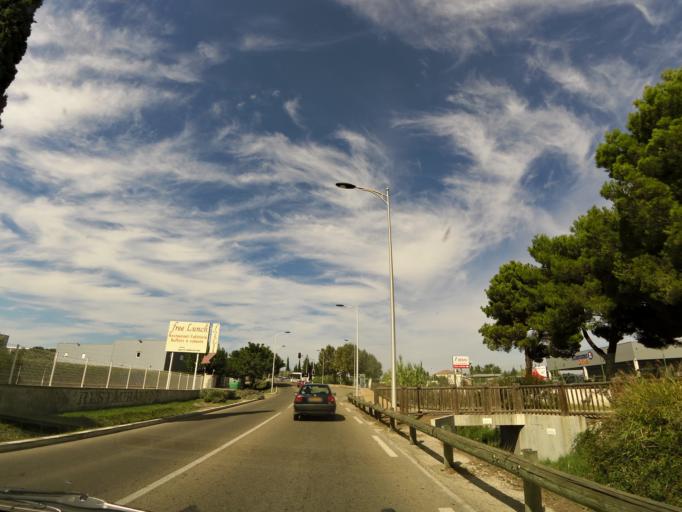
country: FR
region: Languedoc-Roussillon
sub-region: Departement du Gard
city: Caissargues
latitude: 43.8140
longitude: 4.3697
